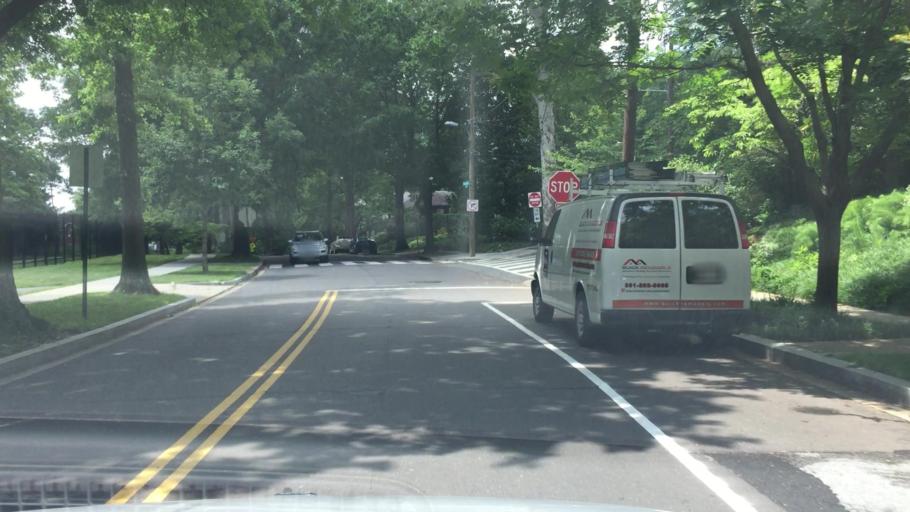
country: US
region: Washington, D.C.
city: Washington, D.C.
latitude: 38.9238
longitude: -77.0692
